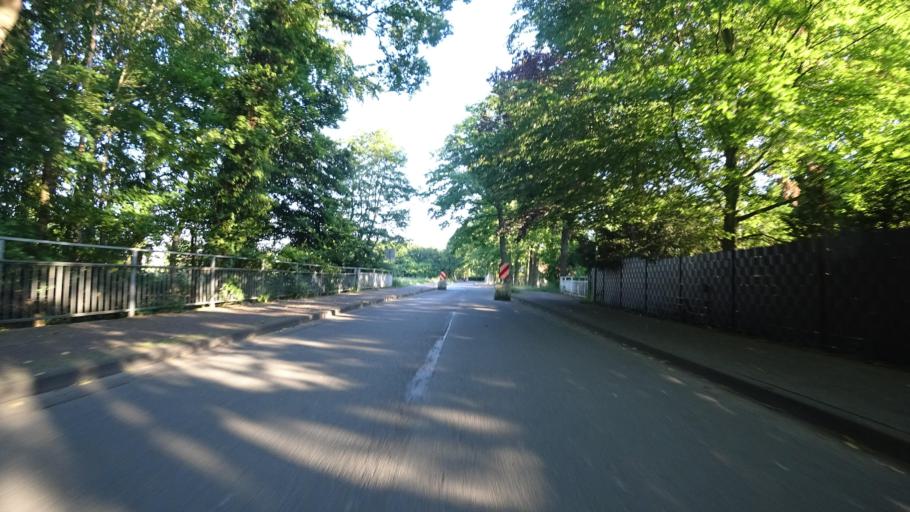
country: DE
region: North Rhine-Westphalia
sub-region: Regierungsbezirk Detmold
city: Guetersloh
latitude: 51.9238
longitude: 8.3969
